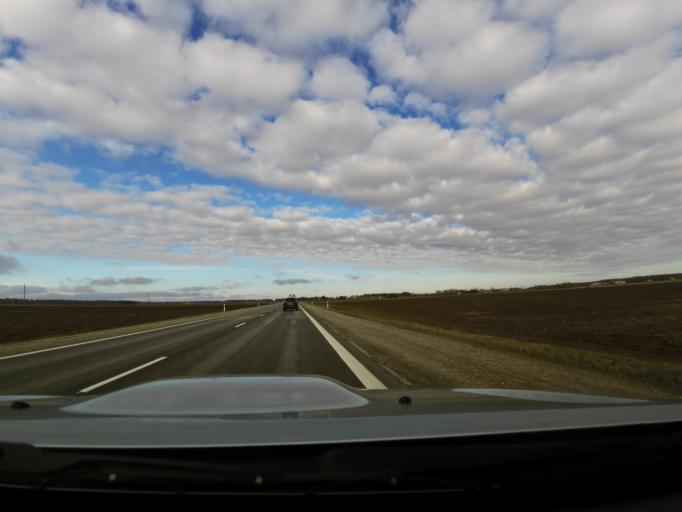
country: LT
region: Panevezys
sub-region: Panevezys City
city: Panevezys
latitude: 55.7585
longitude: 24.1031
